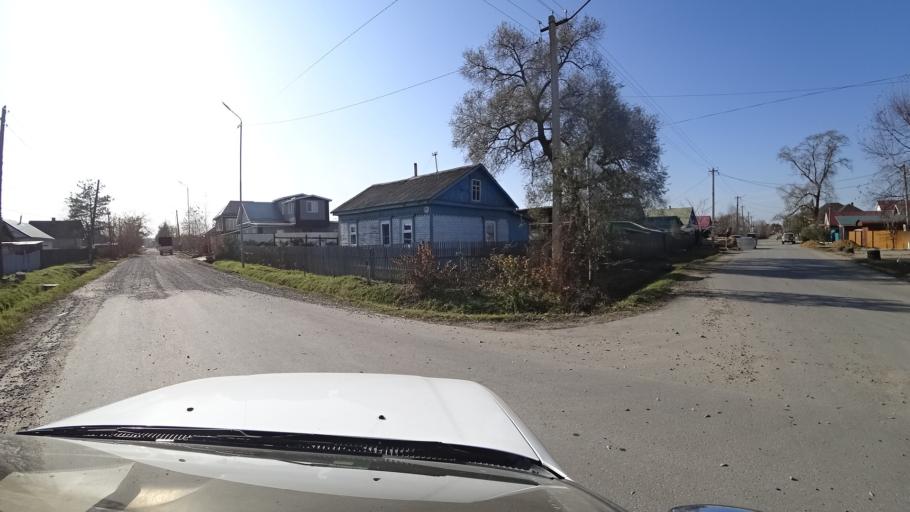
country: RU
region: Primorskiy
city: Dal'nerechensk
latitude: 45.9225
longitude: 133.7266
